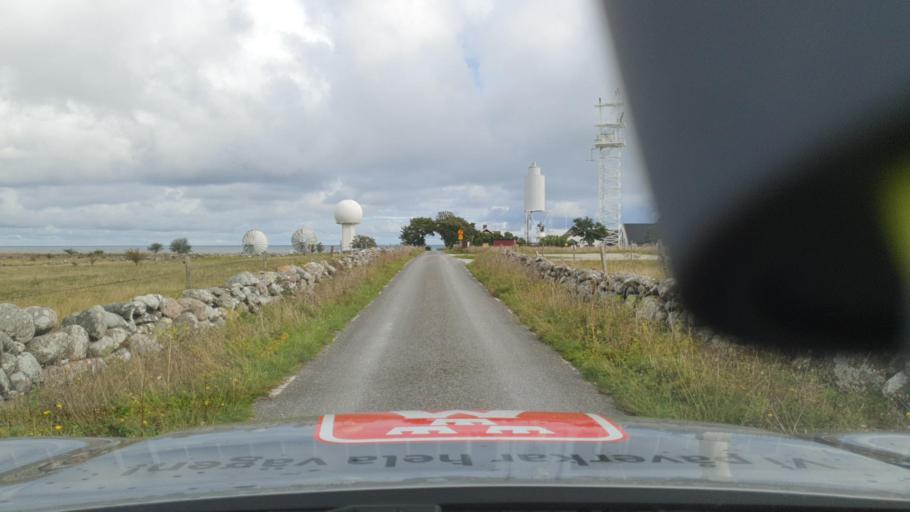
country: SE
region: Gotland
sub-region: Gotland
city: Hemse
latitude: 56.9961
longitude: 18.3921
